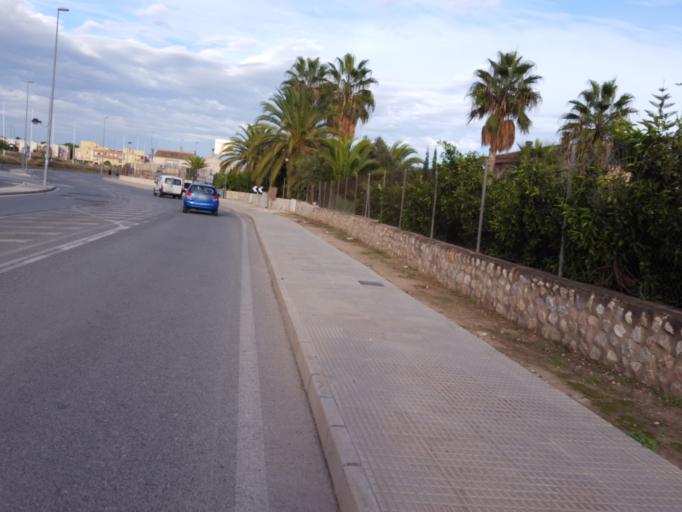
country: ES
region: Murcia
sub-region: Murcia
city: Alcantarilla
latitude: 37.9937
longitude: -1.1803
